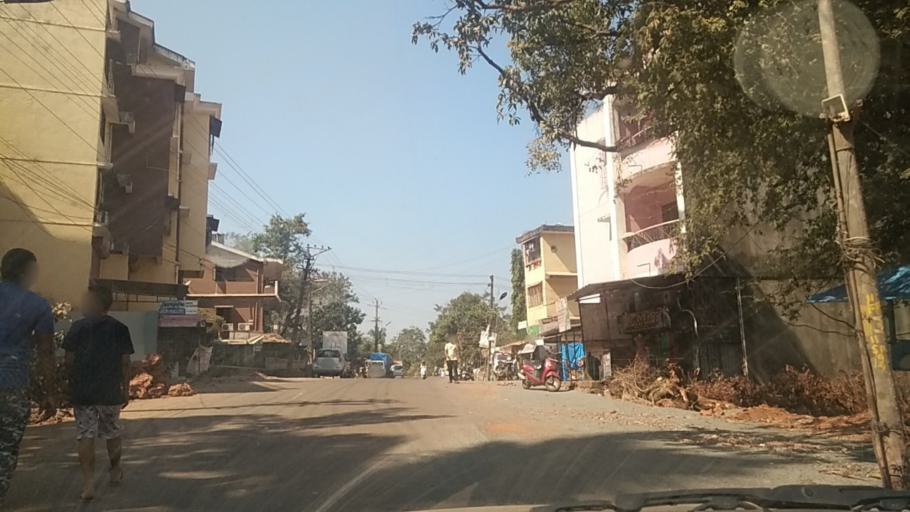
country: IN
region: Goa
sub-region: South Goa
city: Raia
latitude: 15.2991
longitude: 73.9678
